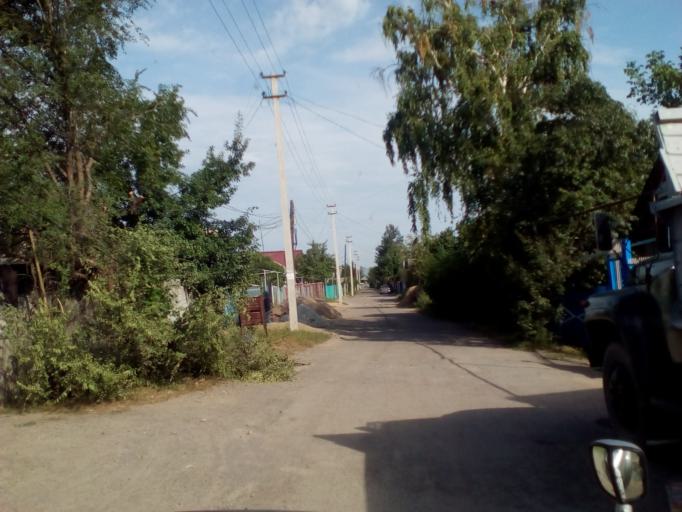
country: KZ
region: Almaty Oblysy
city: Burunday
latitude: 43.1611
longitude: 76.4081
